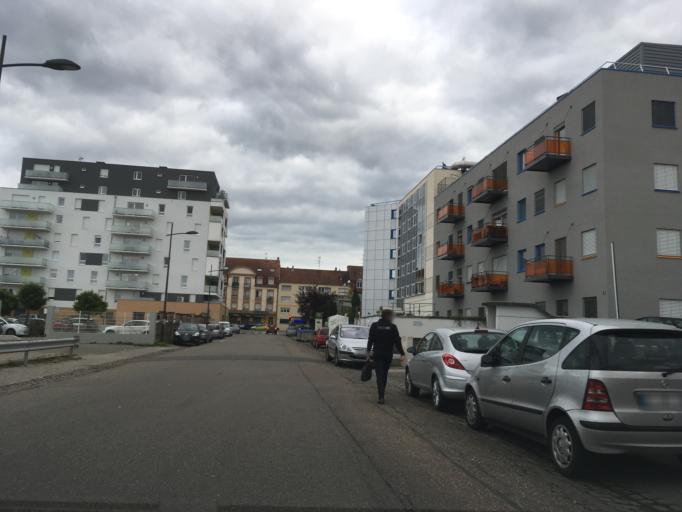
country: FR
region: Alsace
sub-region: Departement du Bas-Rhin
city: Strasbourg
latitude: 48.5567
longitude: 7.7450
